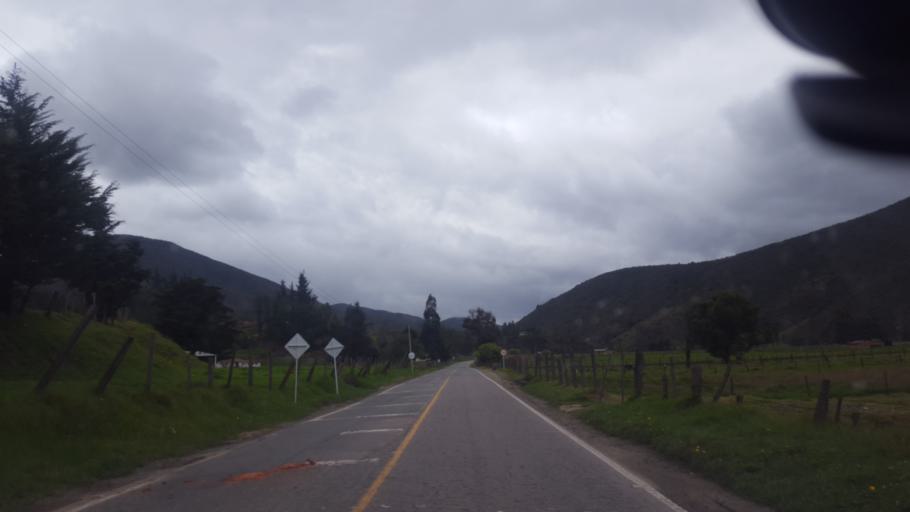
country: CO
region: Boyaca
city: Belen
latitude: 5.9985
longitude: -72.8493
